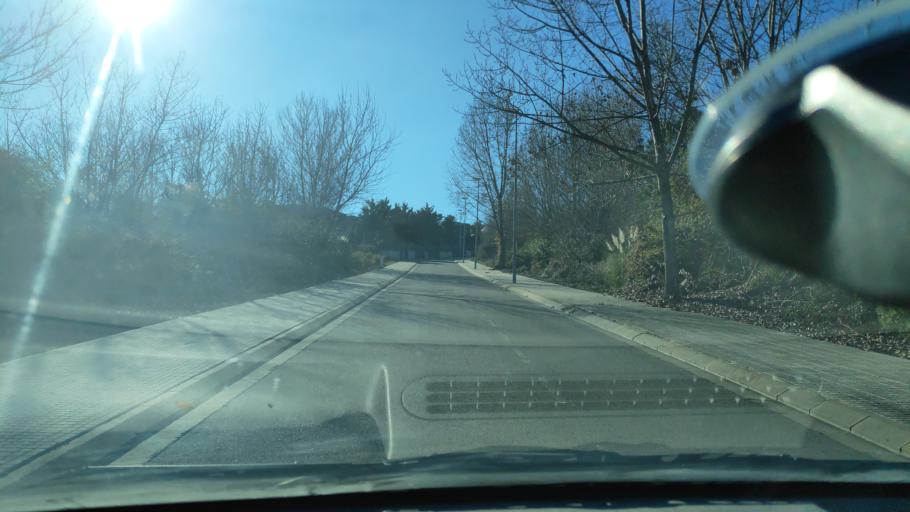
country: ES
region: Catalonia
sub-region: Provincia de Barcelona
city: Sant Quirze del Valles
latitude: 41.5342
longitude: 2.0575
